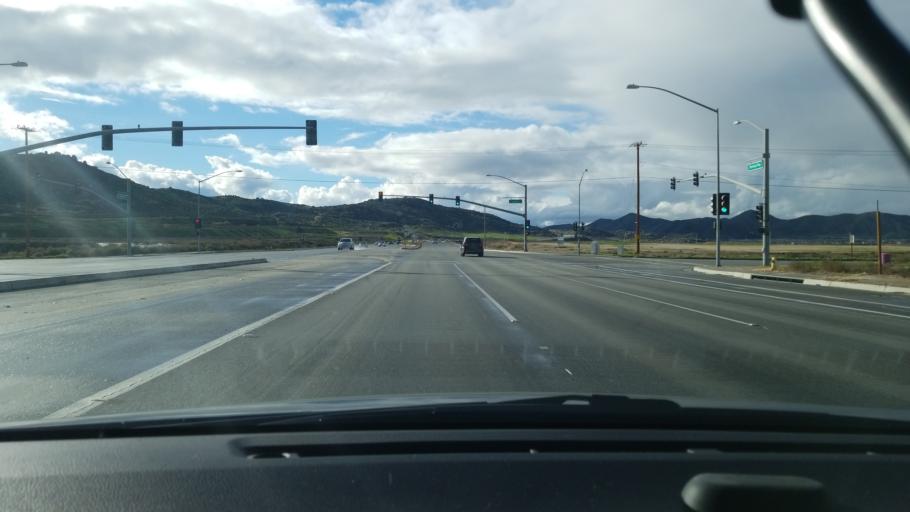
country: US
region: California
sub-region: Riverside County
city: Winchester
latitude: 33.6926
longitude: -117.1188
